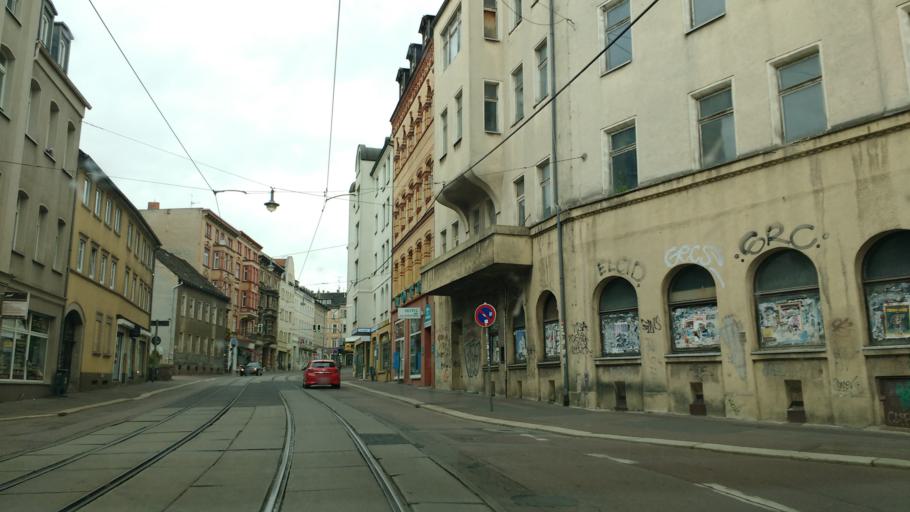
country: DE
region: Saxony-Anhalt
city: Halle (Saale)
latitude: 51.4859
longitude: 11.9745
